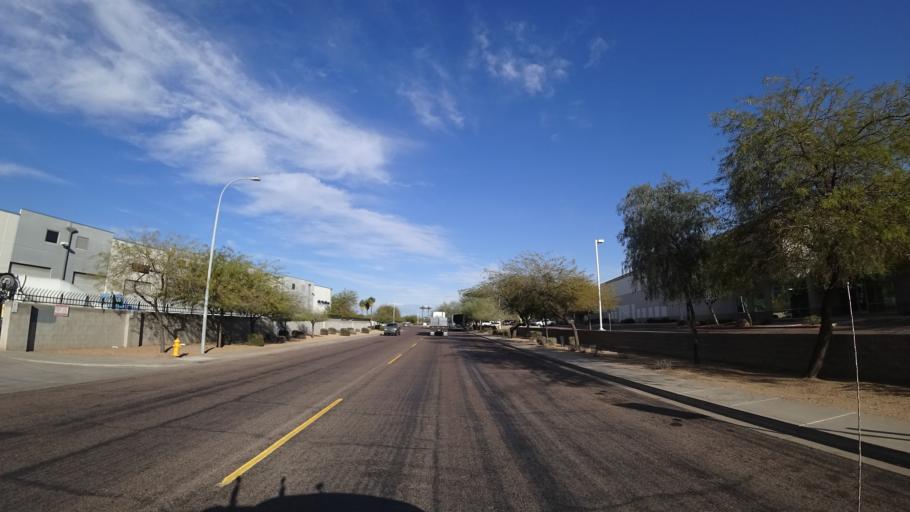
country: US
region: Arizona
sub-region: Maricopa County
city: Glendale
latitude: 33.4611
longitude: -112.1626
